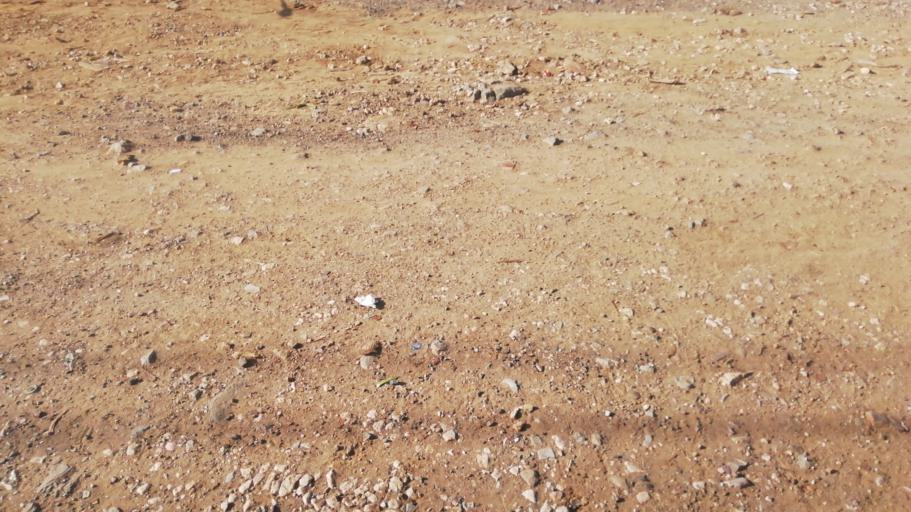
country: CO
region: Cordoba
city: San Antero
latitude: 9.3701
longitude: -75.7630
